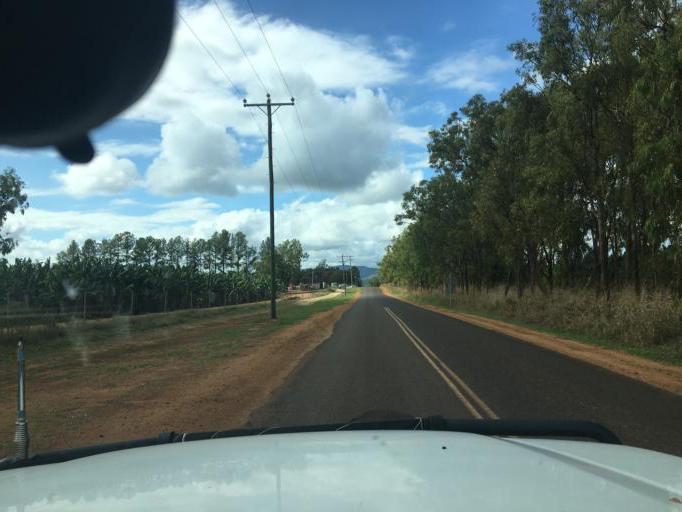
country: AU
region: Queensland
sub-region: Tablelands
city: Mareeba
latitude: -17.0998
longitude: 145.4118
